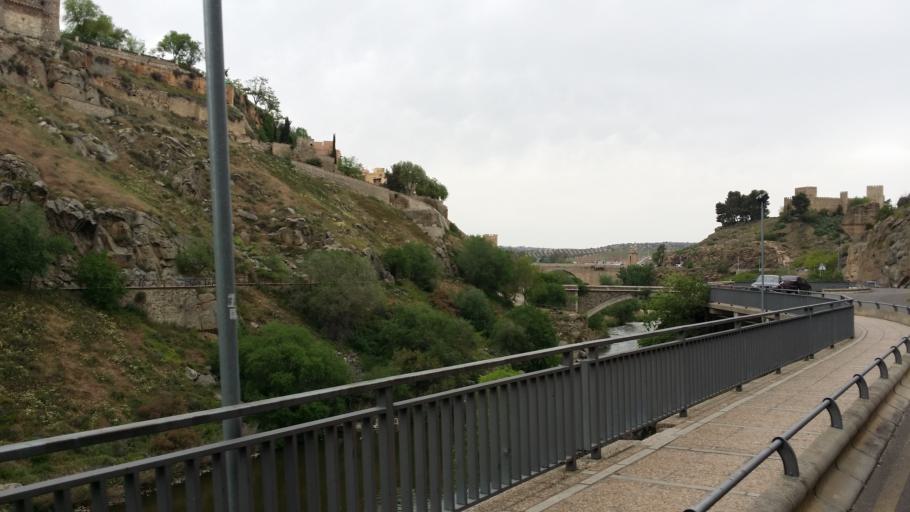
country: ES
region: Castille-La Mancha
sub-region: Province of Toledo
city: Toledo
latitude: 39.8562
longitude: -4.0173
